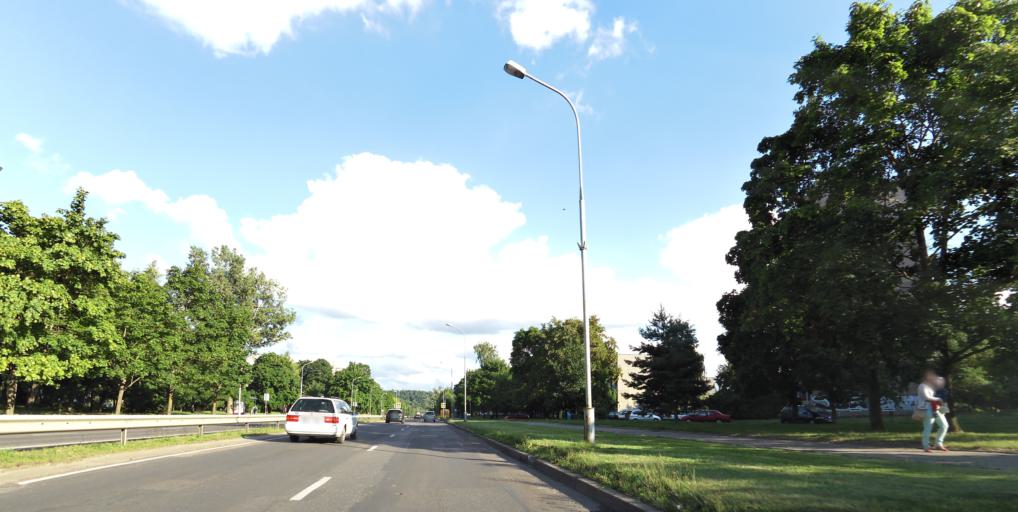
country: LT
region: Vilnius County
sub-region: Vilnius
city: Vilnius
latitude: 54.7012
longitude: 25.2915
